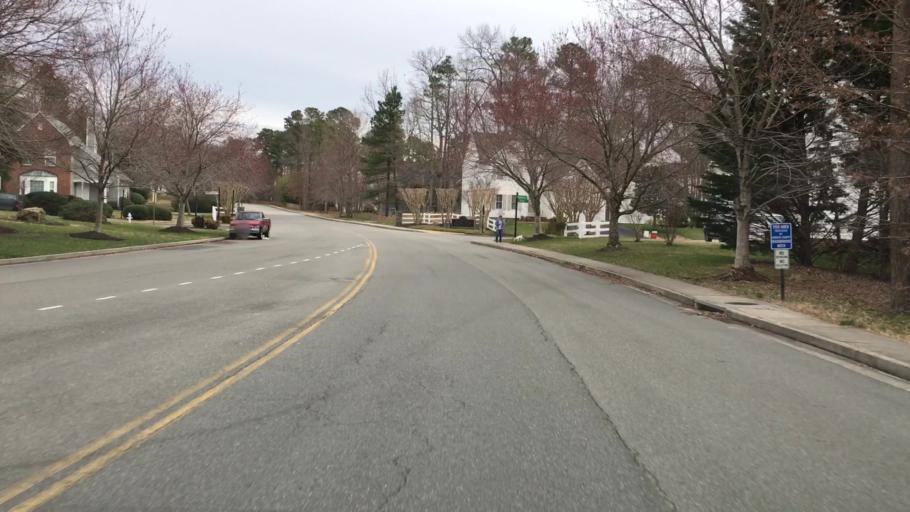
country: US
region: Virginia
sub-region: Henrico County
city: Short Pump
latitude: 37.6488
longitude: -77.5737
